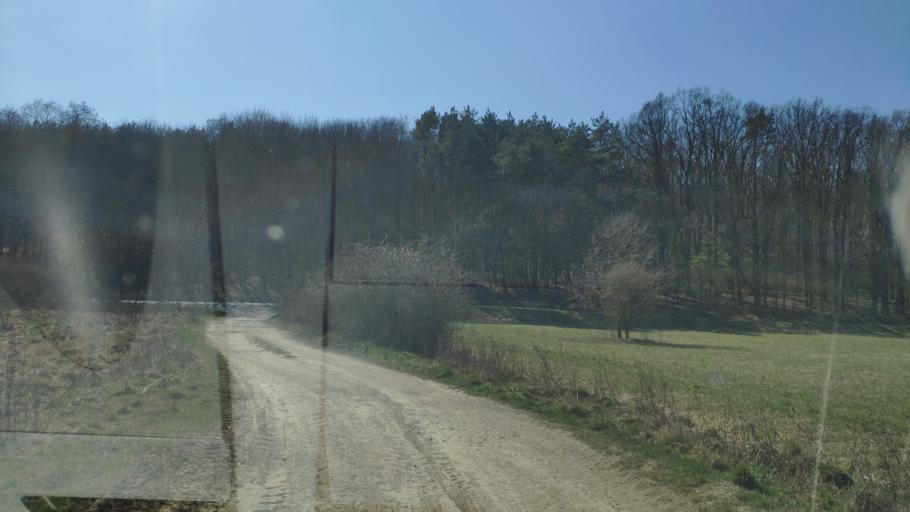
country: SK
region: Kosicky
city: Moldava nad Bodvou
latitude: 48.5667
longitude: 20.9421
